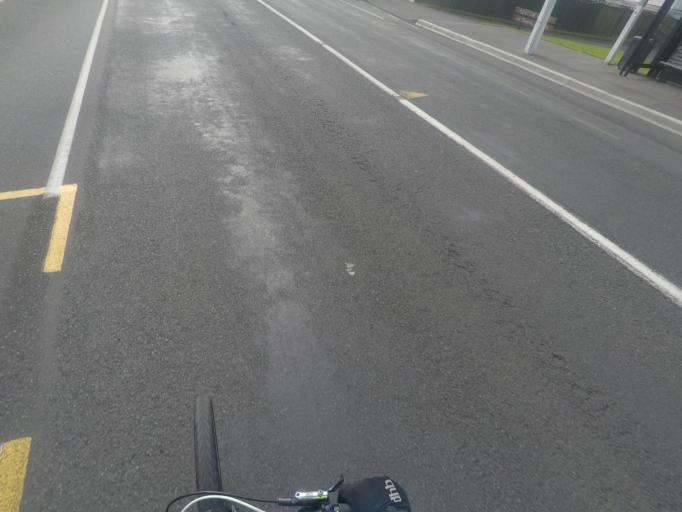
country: NZ
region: Auckland
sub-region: Auckland
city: Auckland
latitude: -36.9163
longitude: 174.7793
